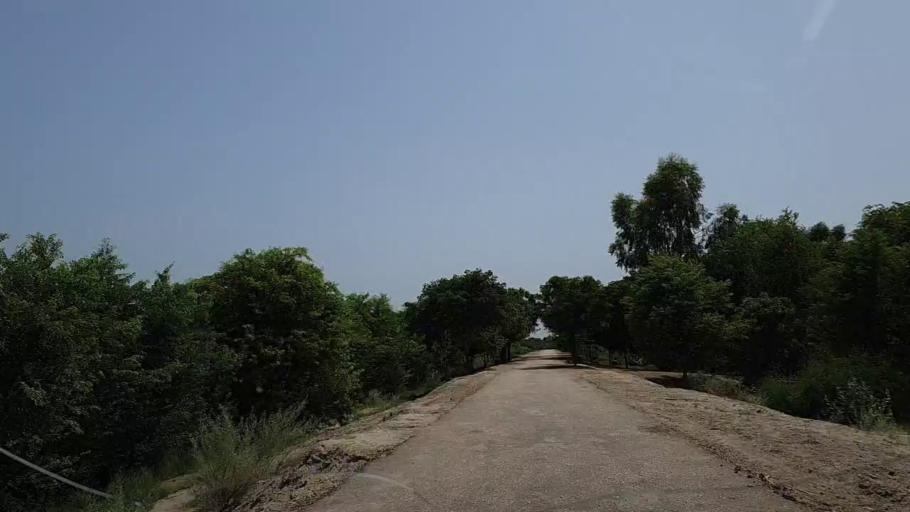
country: PK
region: Sindh
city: Kandiaro
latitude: 27.0487
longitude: 68.1335
